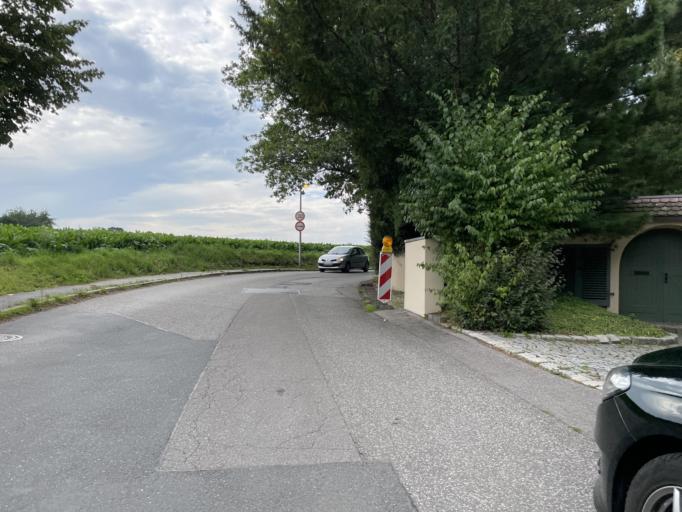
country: DE
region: North Rhine-Westphalia
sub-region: Regierungsbezirk Dusseldorf
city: Heiligenhaus
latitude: 51.3766
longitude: 6.9512
